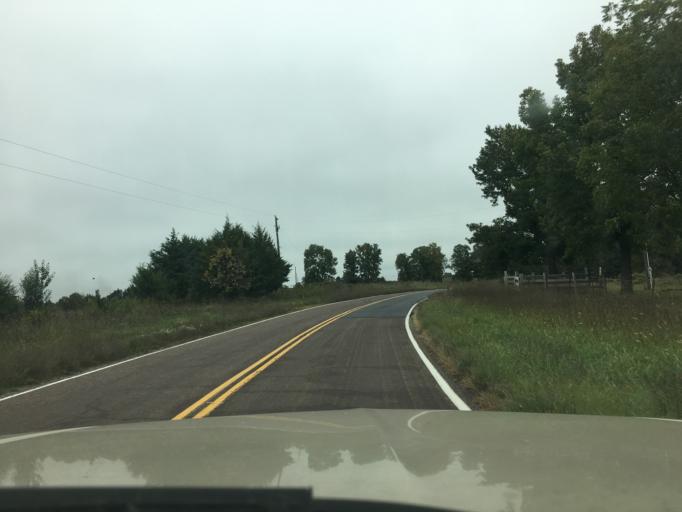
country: US
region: Missouri
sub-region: Crawford County
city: Cuba
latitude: 38.1796
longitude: -91.4894
